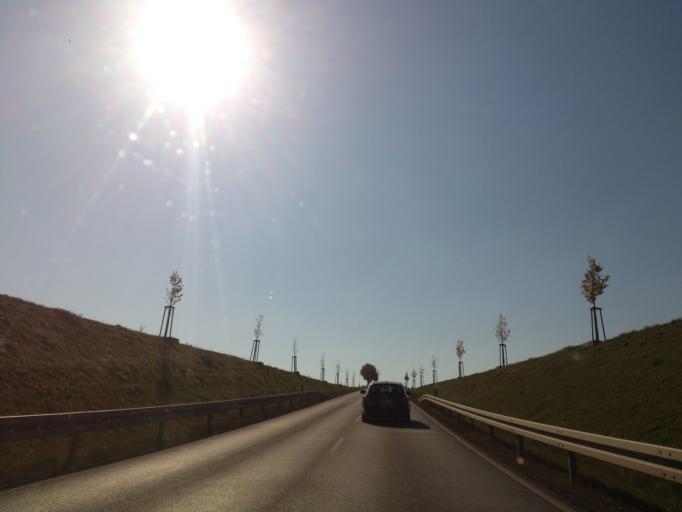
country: DE
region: Hesse
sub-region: Regierungsbezirk Kassel
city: Calden
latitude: 51.3629
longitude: 9.4170
